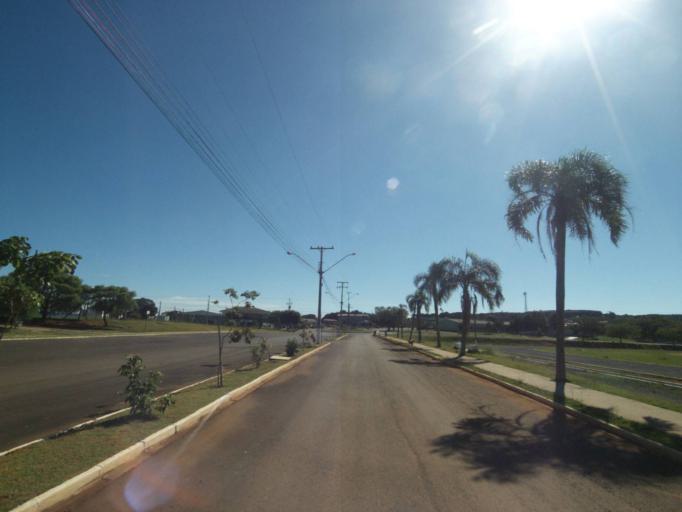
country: BR
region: Parana
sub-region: Pinhao
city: Pinhao
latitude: -25.8347
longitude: -52.0321
